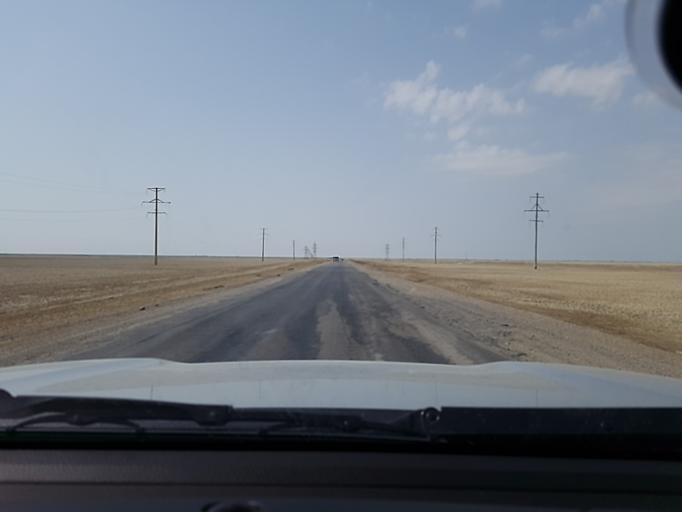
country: TM
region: Balkan
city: Gumdag
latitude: 39.0596
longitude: 54.5844
